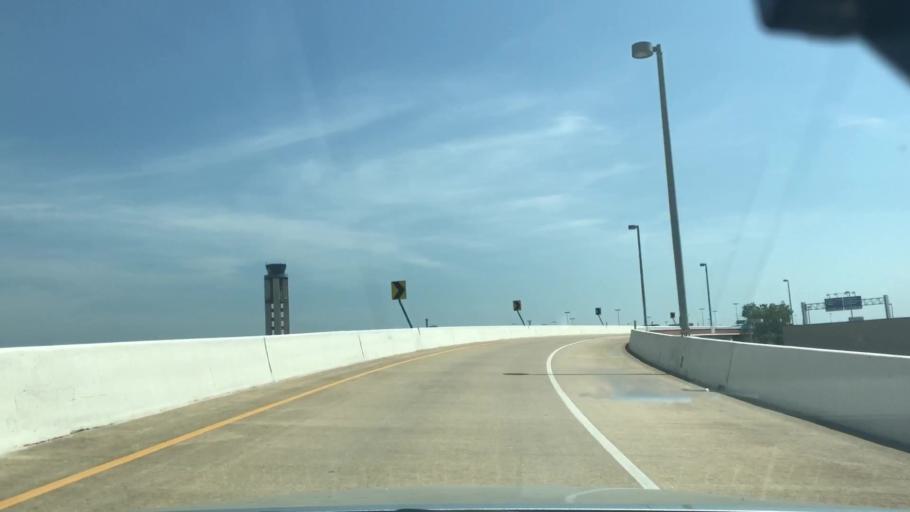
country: US
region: Texas
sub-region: Bexar County
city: Castle Hills
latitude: 29.5245
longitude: -98.4794
